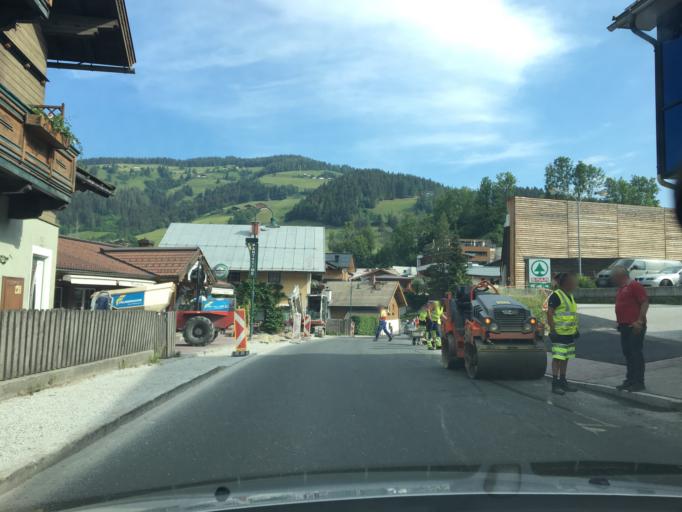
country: AT
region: Salzburg
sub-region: Politischer Bezirk Sankt Johann im Pongau
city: Wagrain
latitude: 47.3311
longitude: 13.2978
